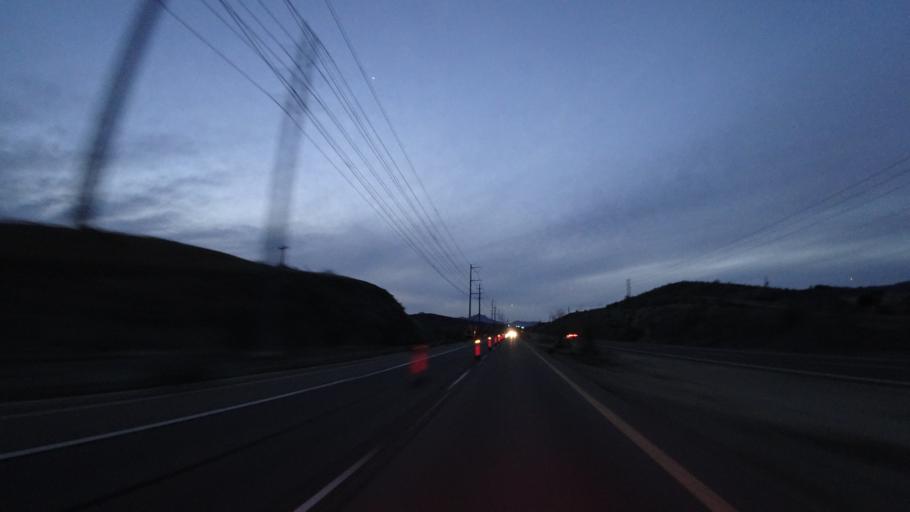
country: US
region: Arizona
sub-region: Maricopa County
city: Guadalupe
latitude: 33.2910
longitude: -112.0540
